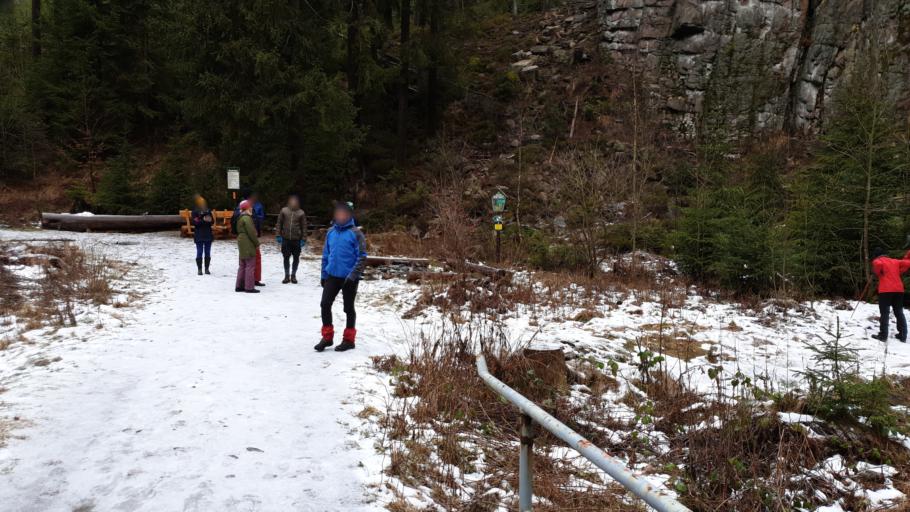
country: DE
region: Saxony
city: Johanngeorgenstadt
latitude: 50.4517
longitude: 12.6958
